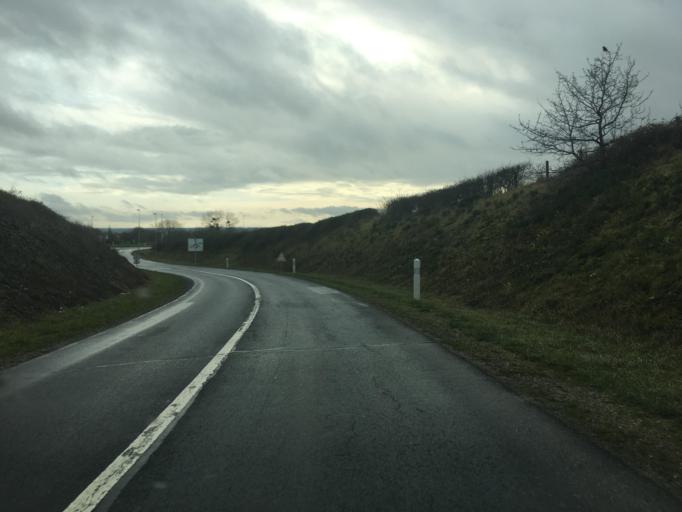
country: FR
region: Lower Normandy
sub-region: Departement du Calvados
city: Isigny-sur-Mer
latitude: 49.3327
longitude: -1.0764
